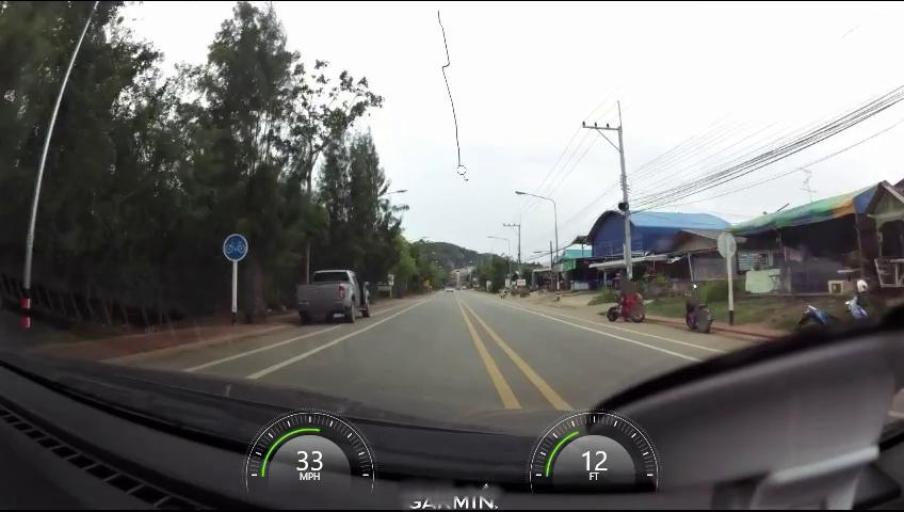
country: TH
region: Prachuap Khiri Khan
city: Hua Hin
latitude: 12.4652
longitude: 99.9741
